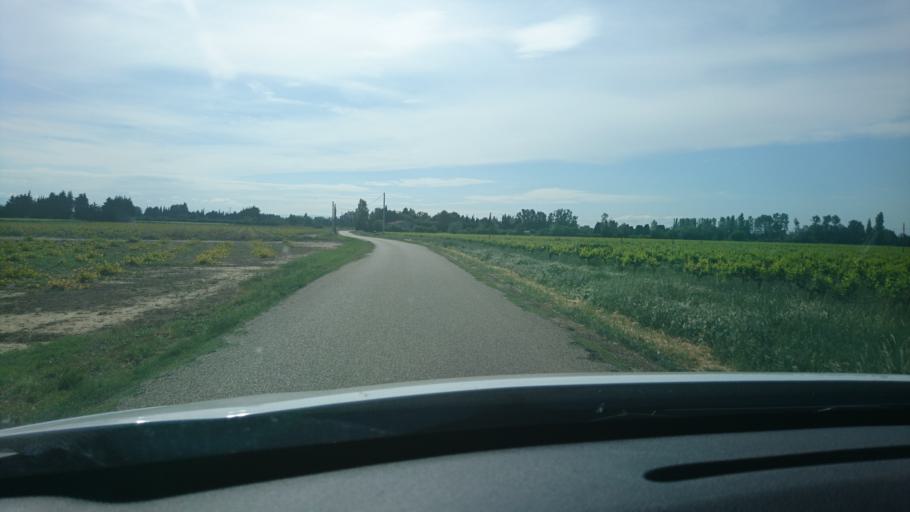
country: FR
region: Provence-Alpes-Cote d'Azur
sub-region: Departement du Vaucluse
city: Jonquieres
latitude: 44.1338
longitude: 4.8802
